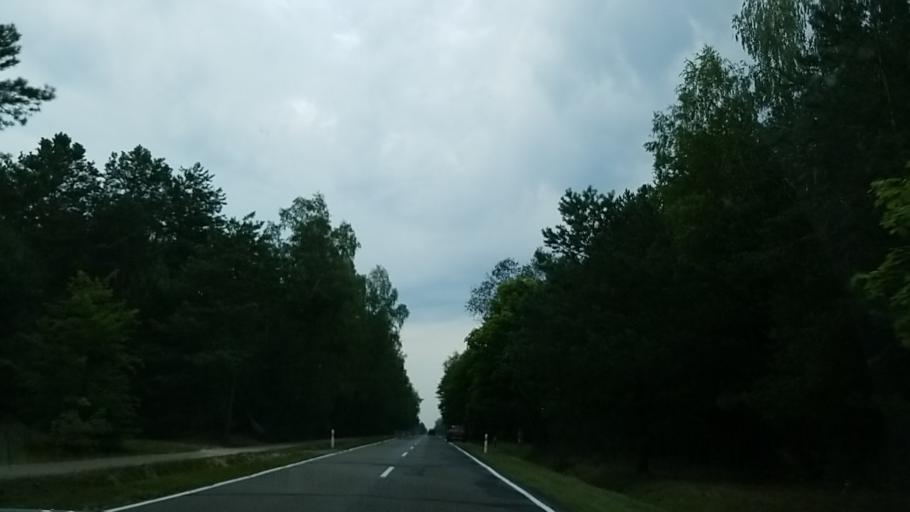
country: PL
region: Lublin Voivodeship
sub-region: Powiat bialski
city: Slawatycze
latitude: 51.7258
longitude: 23.5123
